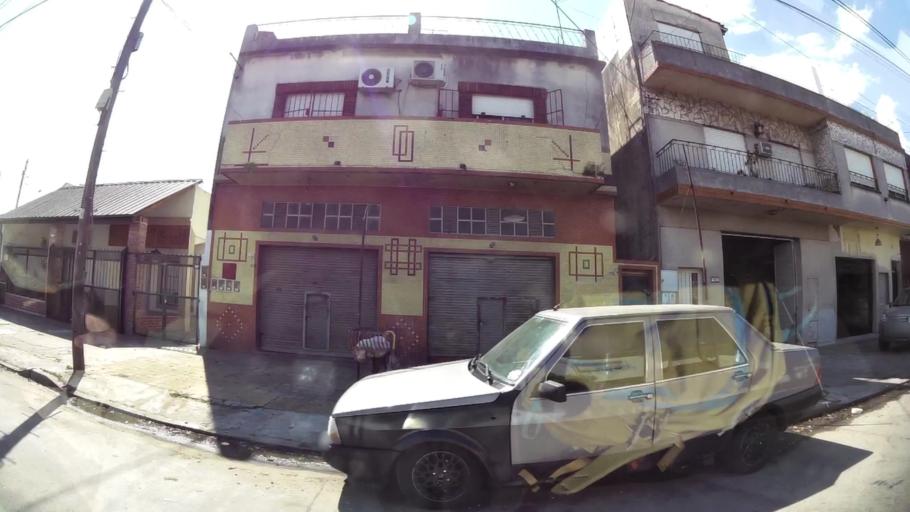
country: AR
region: Buenos Aires
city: San Justo
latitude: -34.6552
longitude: -58.5340
